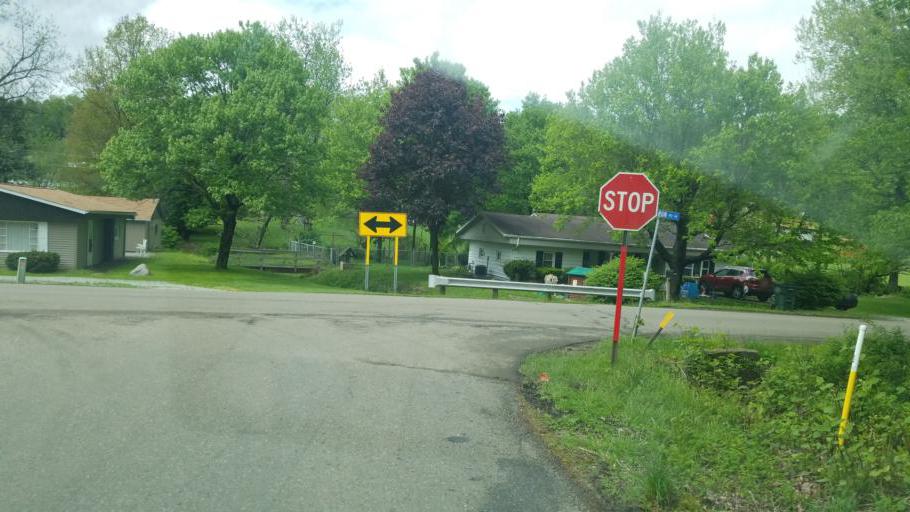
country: US
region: Ohio
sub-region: Tuscarawas County
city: New Philadelphia
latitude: 40.5290
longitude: -81.4210
